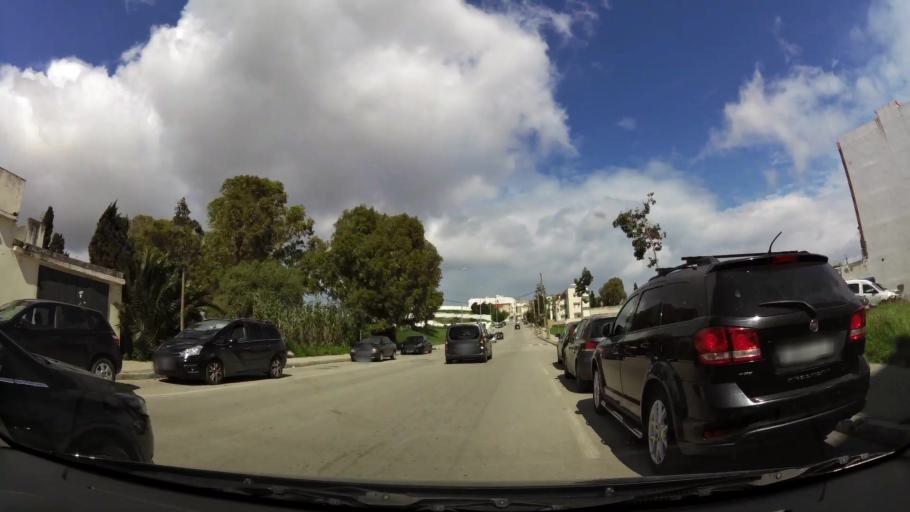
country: MA
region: Tanger-Tetouan
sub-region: Tanger-Assilah
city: Tangier
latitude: 35.7722
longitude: -5.8314
